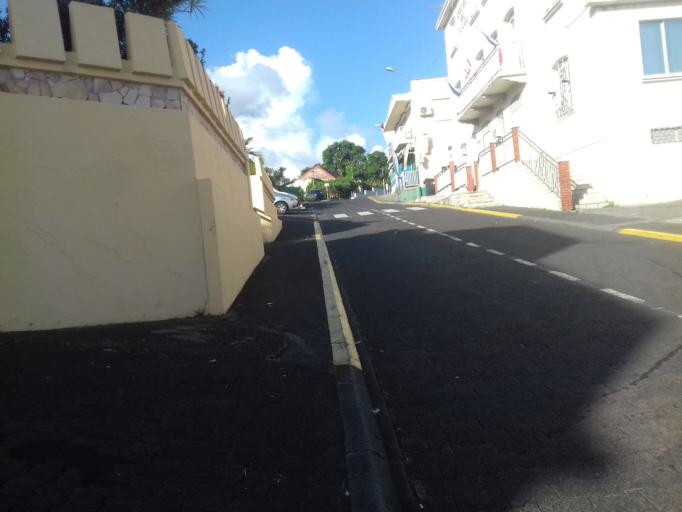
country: MQ
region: Martinique
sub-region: Martinique
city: Fort-de-France
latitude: 14.6159
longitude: -61.1016
